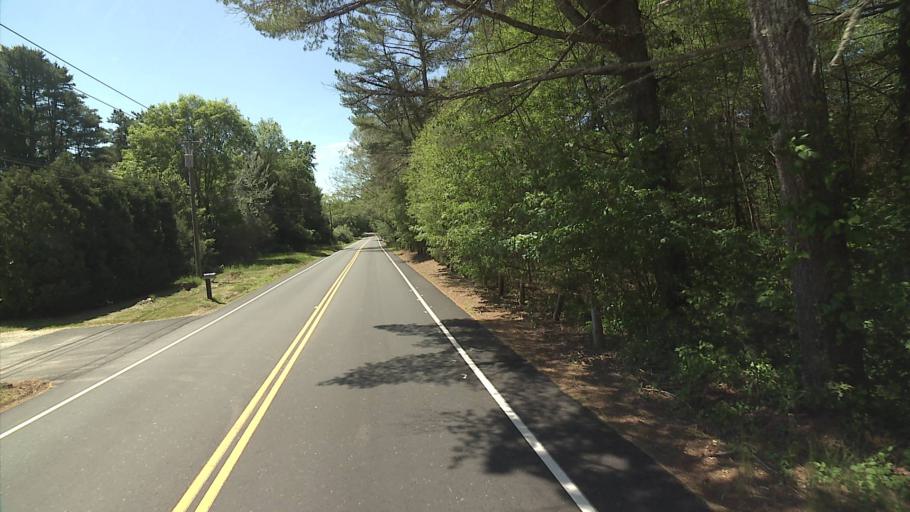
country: US
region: Connecticut
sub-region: Windham County
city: Plainfield
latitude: 41.5892
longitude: -71.8556
